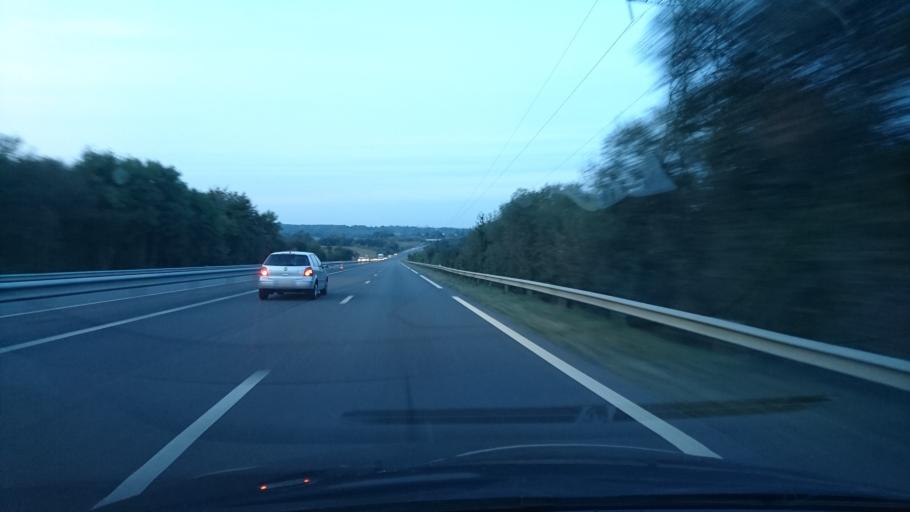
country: FR
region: Brittany
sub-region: Departement d'Ille-et-Vilaine
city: Guichen
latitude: 47.9958
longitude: -1.8127
